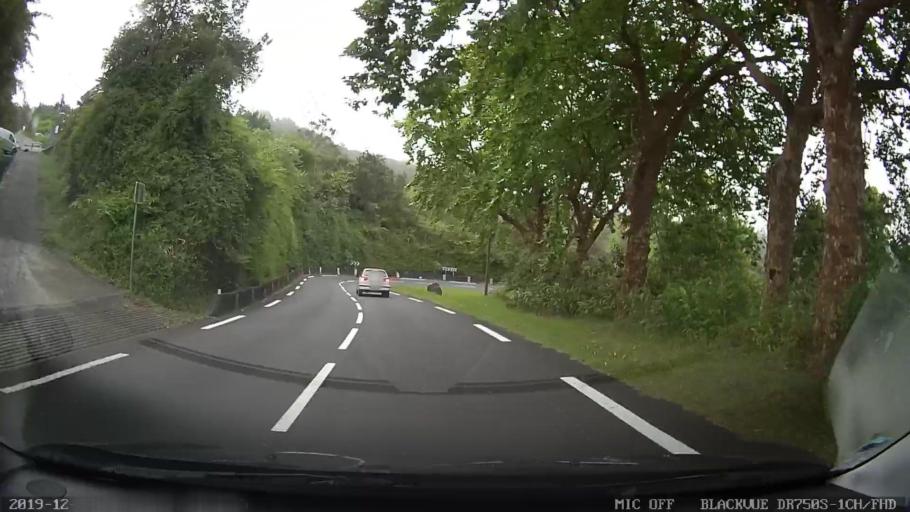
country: RE
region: Reunion
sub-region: Reunion
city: Cilaos
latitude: -21.1497
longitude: 55.6148
